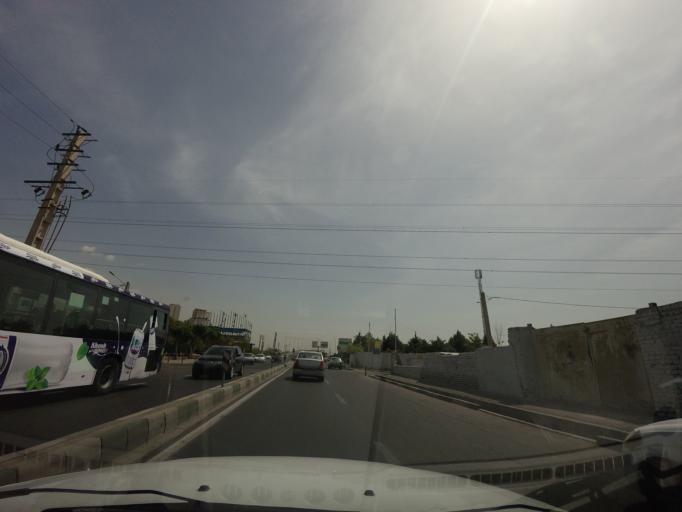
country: IR
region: Tehran
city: Shahr-e Qods
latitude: 35.7459
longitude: 51.2504
